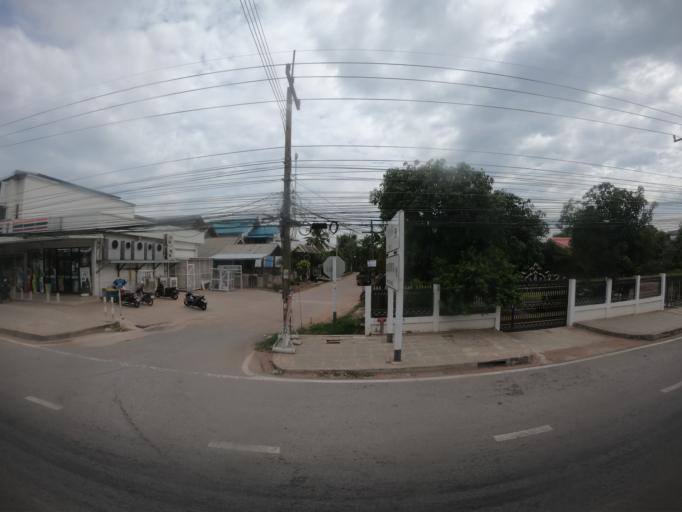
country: TH
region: Maha Sarakham
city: Kantharawichai
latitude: 16.3230
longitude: 103.2991
